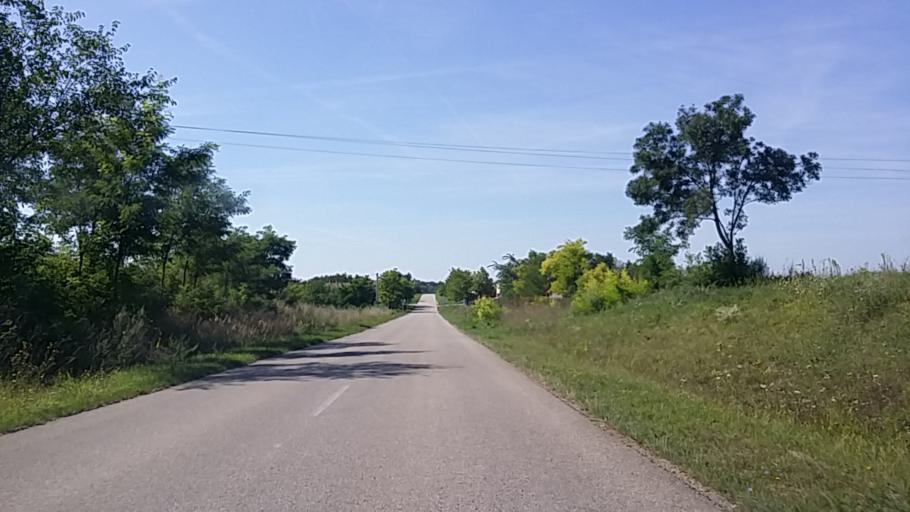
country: HU
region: Fejer
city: Deg
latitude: 46.8834
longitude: 18.4473
